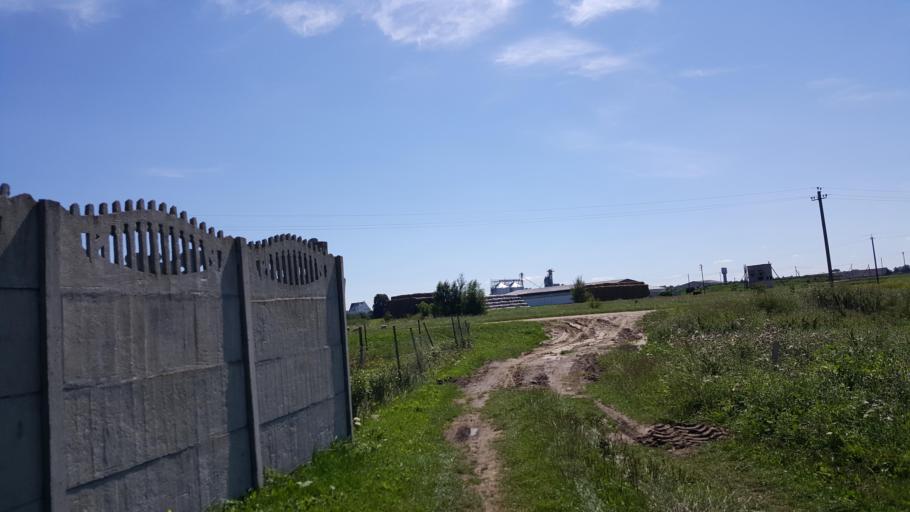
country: BY
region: Brest
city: Charnawchytsy
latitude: 52.2215
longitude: 23.7318
